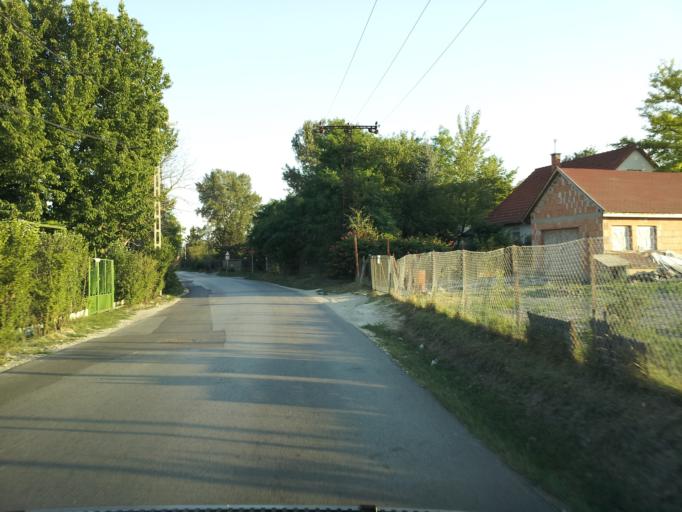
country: HU
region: Pest
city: Szigetszentmiklos
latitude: 47.3221
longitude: 19.0322
